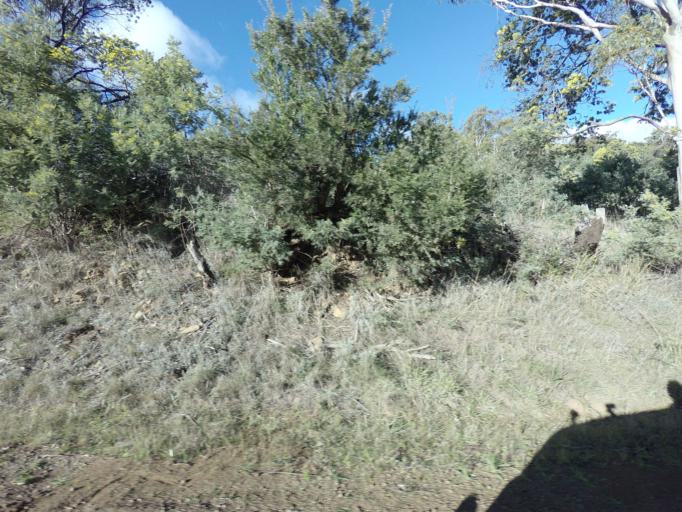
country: AU
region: Tasmania
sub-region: Derwent Valley
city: New Norfolk
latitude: -42.7037
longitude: 146.9968
